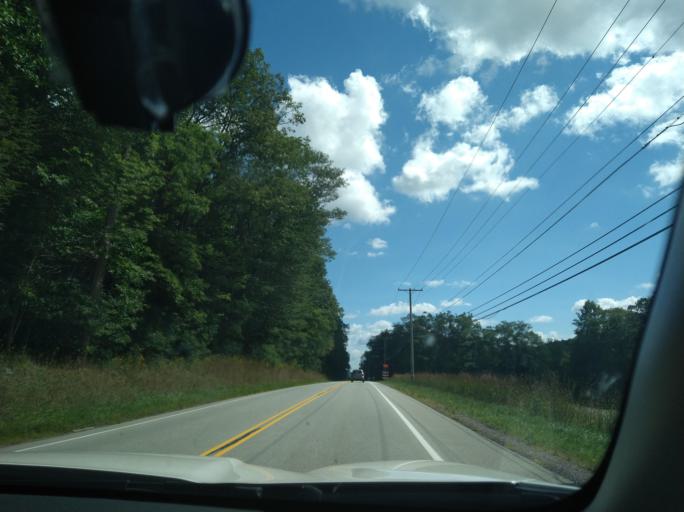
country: US
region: Pennsylvania
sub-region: Somerset County
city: Somerset
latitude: 40.0584
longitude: -79.2248
